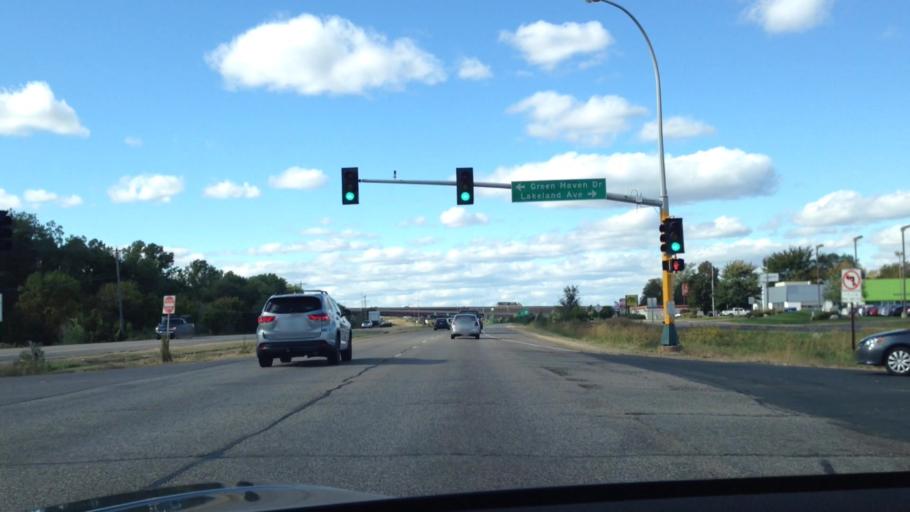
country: US
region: Minnesota
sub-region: Hennepin County
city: Osseo
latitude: 45.1008
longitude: -93.3889
